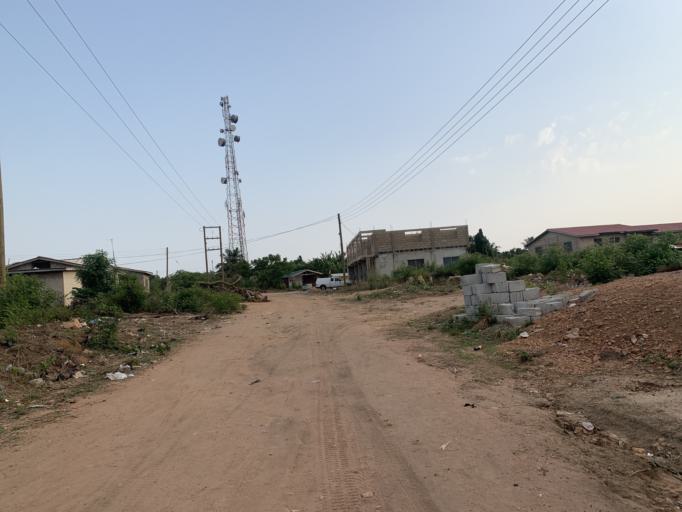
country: GH
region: Central
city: Winneba
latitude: 5.3606
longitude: -0.6272
